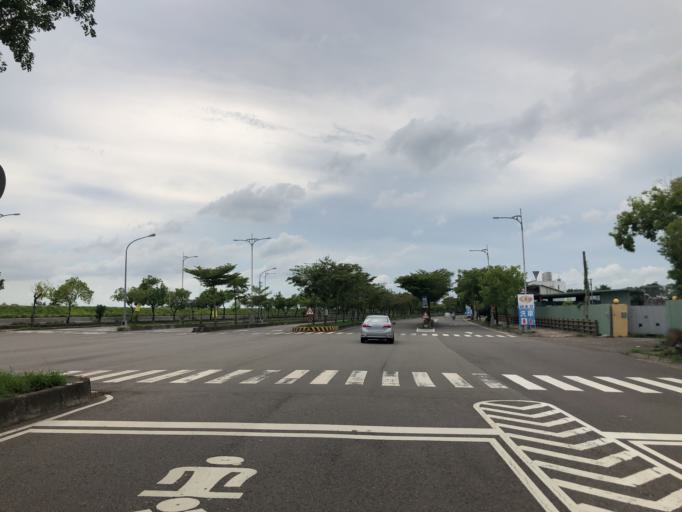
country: TW
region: Taiwan
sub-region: Taichung City
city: Taichung
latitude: 24.0837
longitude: 120.6617
